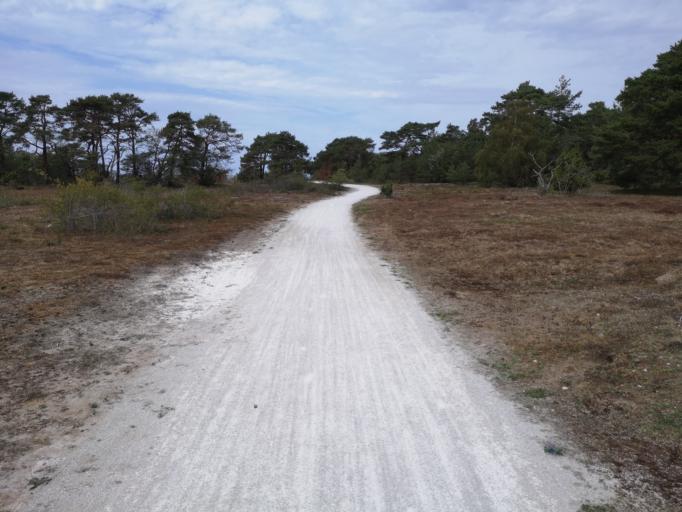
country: SE
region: Gotland
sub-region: Gotland
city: Vibble
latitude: 57.6143
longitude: 18.2601
